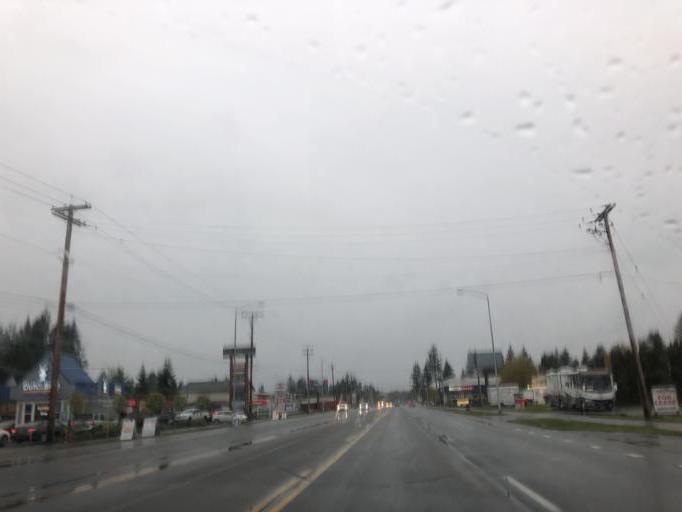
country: US
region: Washington
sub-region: Thurston County
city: Tanglewilde-Thompson Place
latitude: 47.0530
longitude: -122.7835
